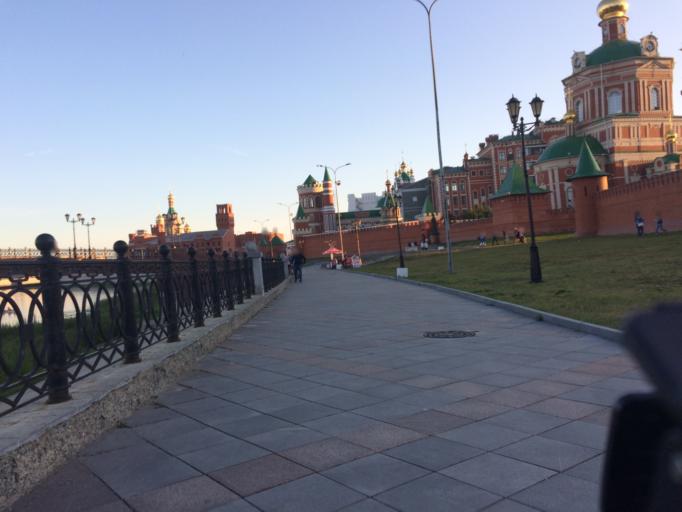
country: RU
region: Mariy-El
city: Yoshkar-Ola
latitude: 56.6378
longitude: 47.9041
